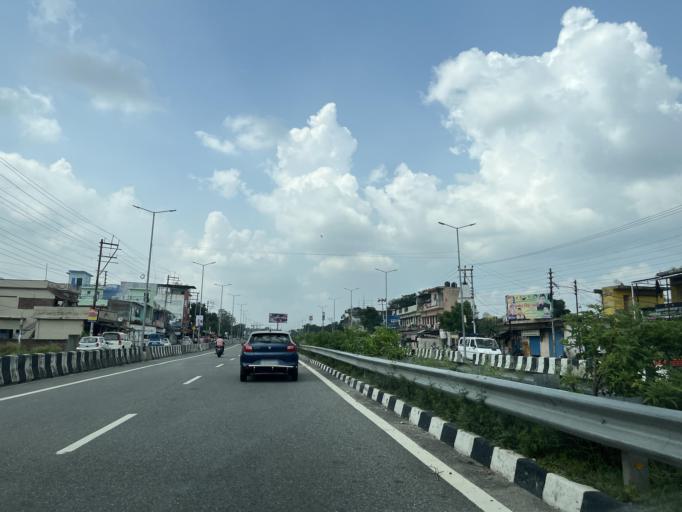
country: IN
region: Uttarakhand
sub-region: Dehradun
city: Raipur
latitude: 30.2583
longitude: 78.0902
